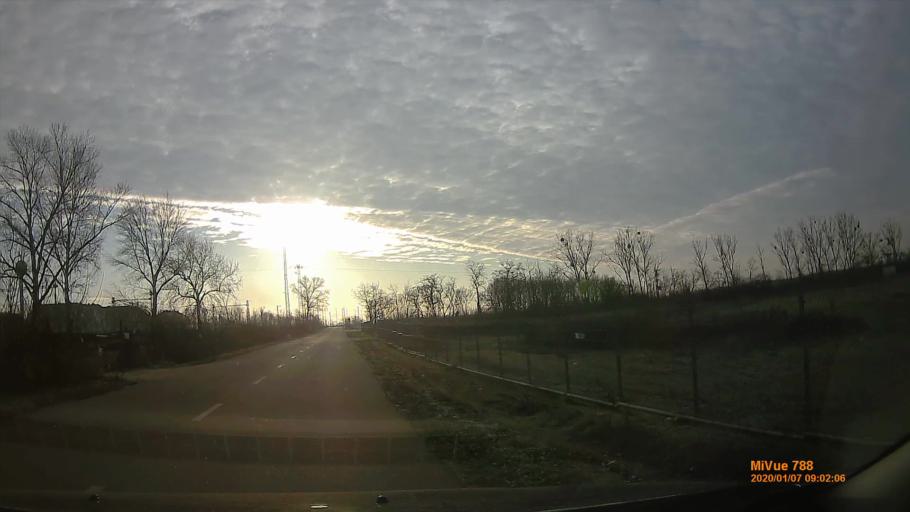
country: HU
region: Gyor-Moson-Sopron
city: Rajka
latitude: 47.9905
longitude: 17.1939
